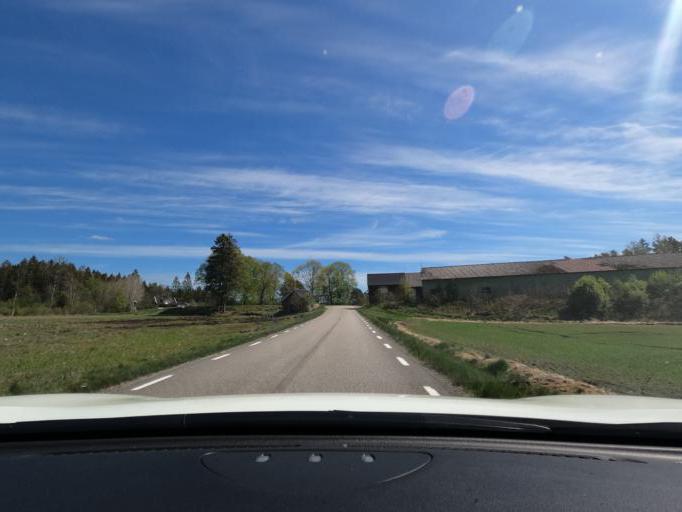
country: SE
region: Vaestra Goetaland
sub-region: Marks Kommun
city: Horred
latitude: 57.4245
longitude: 12.3519
